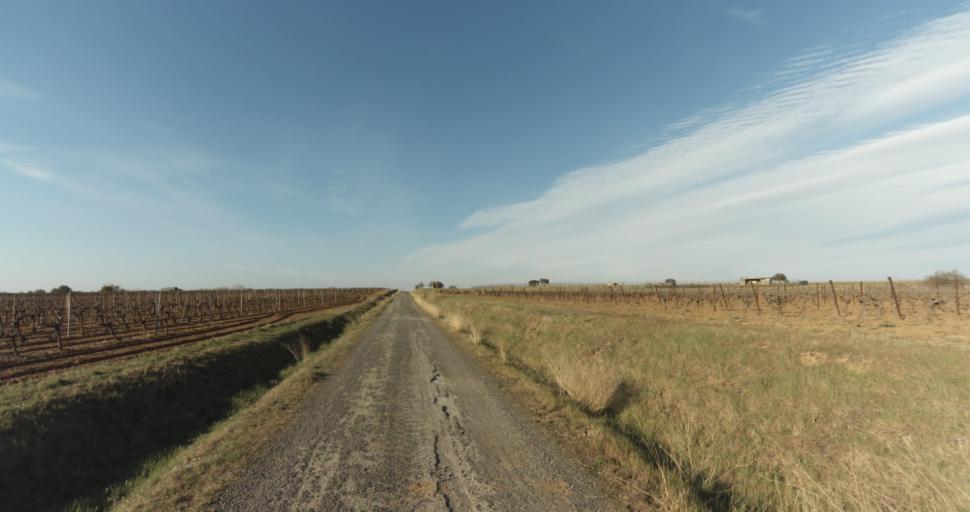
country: FR
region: Languedoc-Roussillon
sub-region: Departement de l'Herault
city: Marseillan
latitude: 43.3762
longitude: 3.5232
